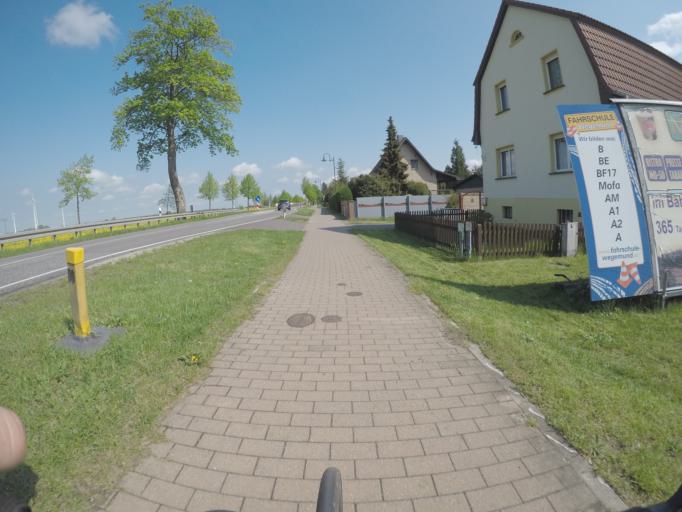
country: DE
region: Brandenburg
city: Wandlitz
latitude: 52.7791
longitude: 13.4791
